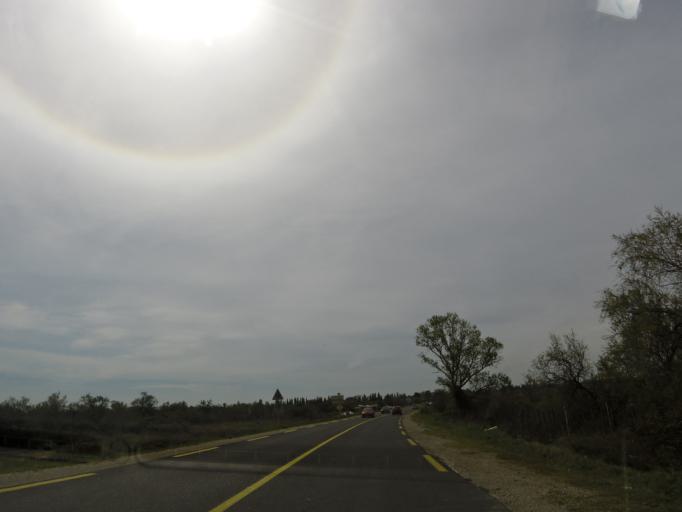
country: FR
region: Languedoc-Roussillon
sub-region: Departement de l'Herault
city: La Grande-Motte
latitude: 43.5815
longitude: 4.1035
